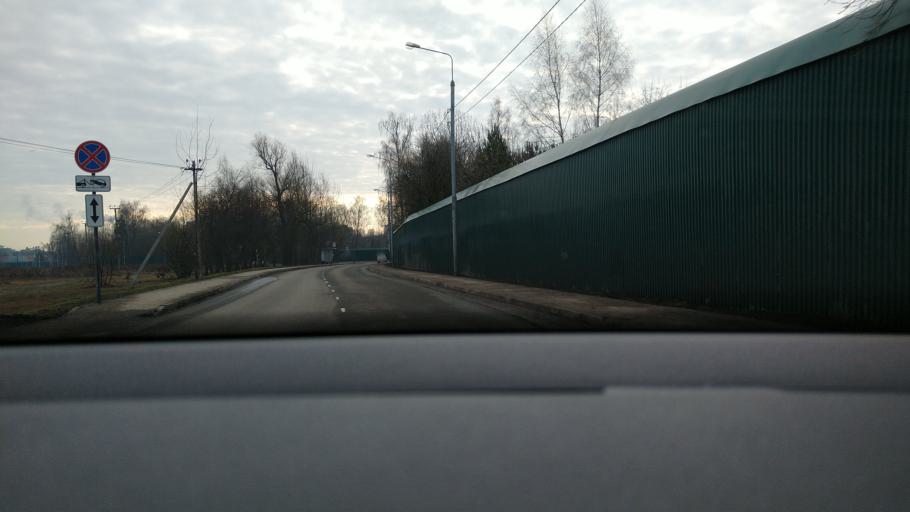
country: RU
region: Moskovskaya
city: Vatutinki
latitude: 55.5150
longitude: 37.3390
